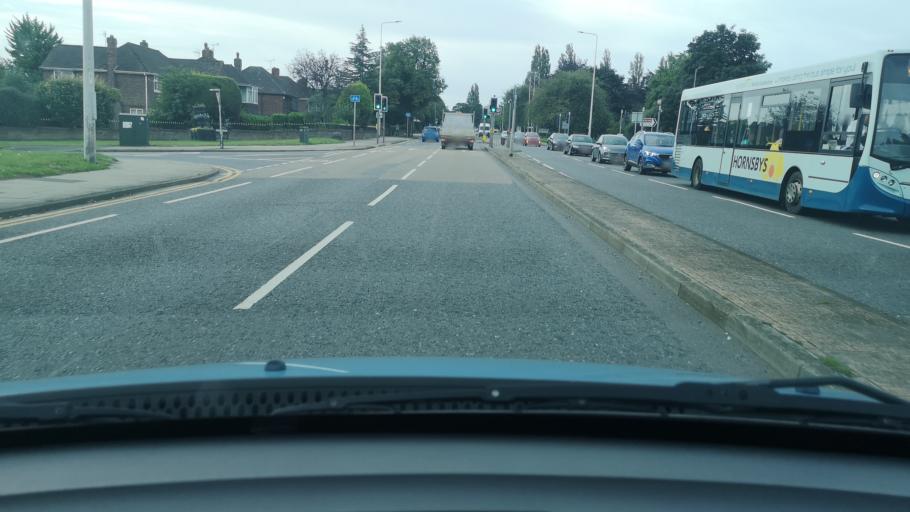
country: GB
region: England
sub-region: North Lincolnshire
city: Scunthorpe
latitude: 53.5825
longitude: -0.6535
